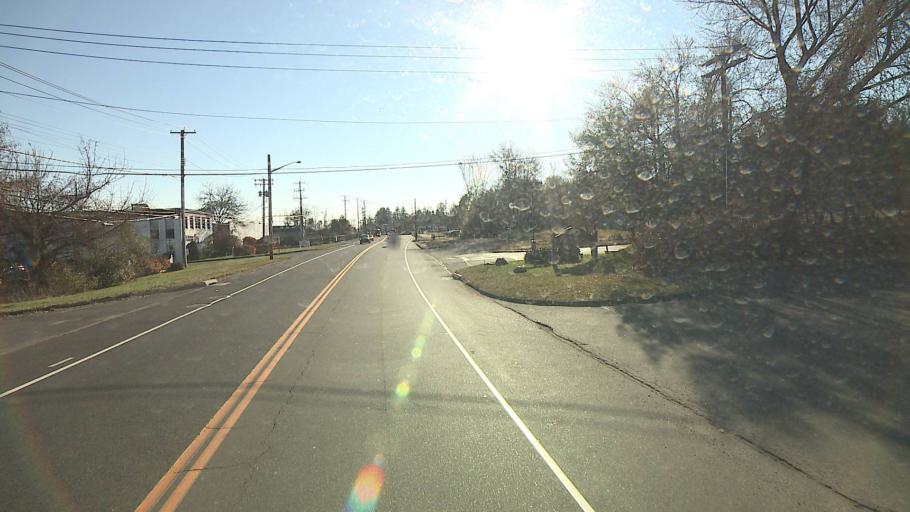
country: US
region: Connecticut
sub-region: New Haven County
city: Hamden
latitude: 41.3663
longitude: -72.8871
